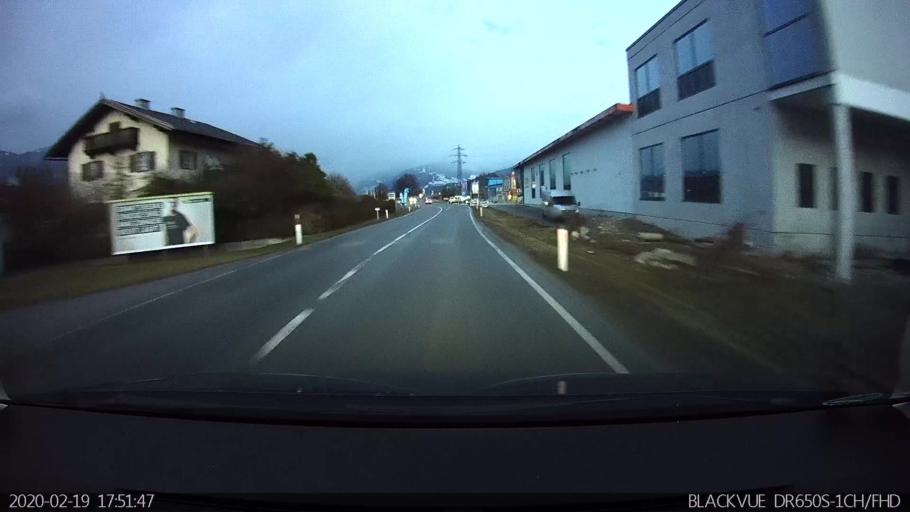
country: AT
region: Tyrol
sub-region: Politischer Bezirk Innsbruck Land
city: Volders
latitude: 47.2834
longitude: 11.5483
